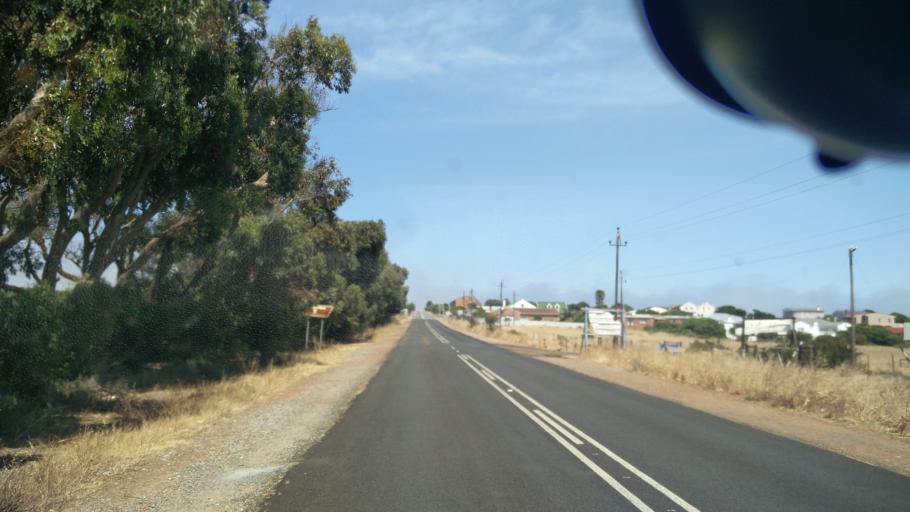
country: ZA
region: Western Cape
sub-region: City of Cape Town
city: Atlantis
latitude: -33.3432
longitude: 18.1702
